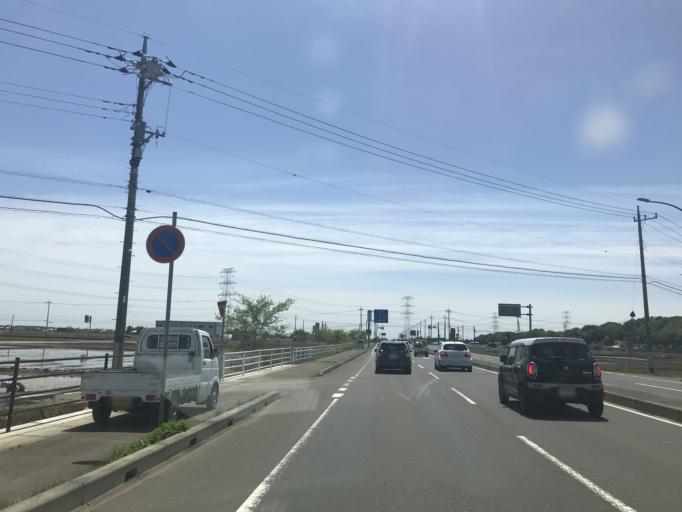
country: JP
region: Ibaraki
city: Shimodate
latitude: 36.2510
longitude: 139.9831
